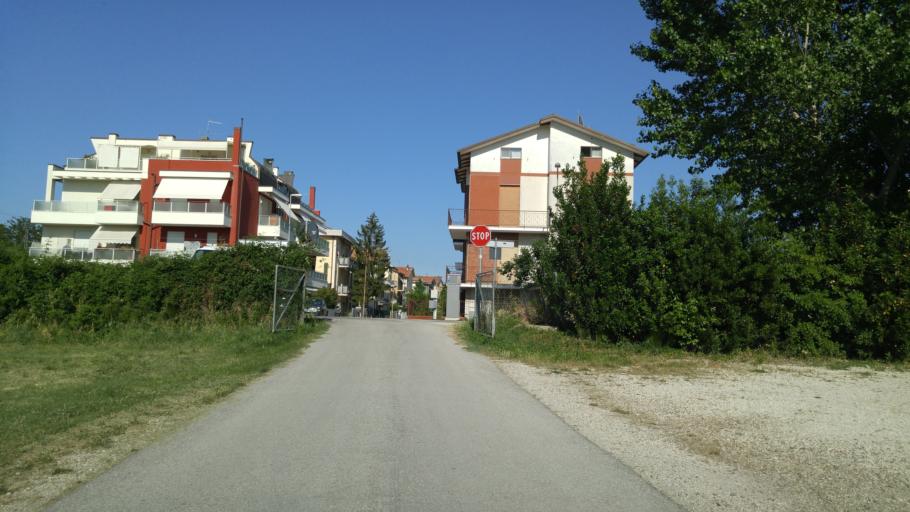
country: IT
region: The Marches
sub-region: Provincia di Pesaro e Urbino
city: Pesaro
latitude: 43.9094
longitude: 12.8848
